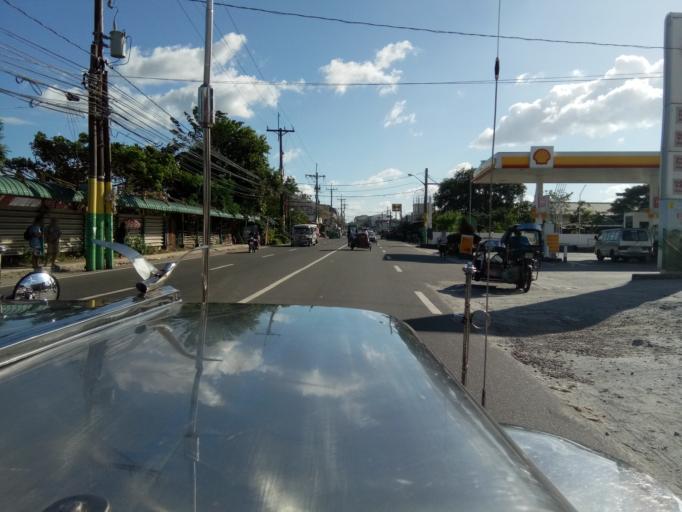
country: PH
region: Calabarzon
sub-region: Province of Cavite
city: Dasmarinas
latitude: 14.3527
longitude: 120.9811
